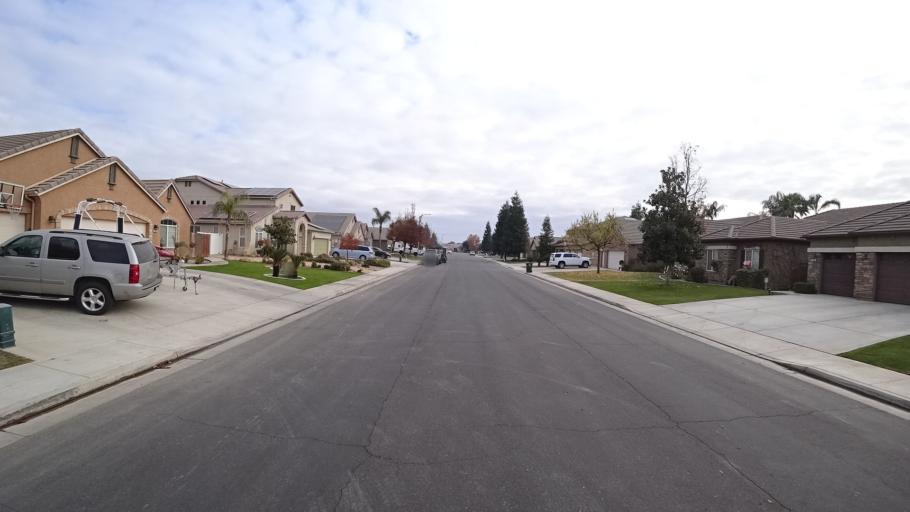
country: US
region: California
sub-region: Kern County
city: Rosedale
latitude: 35.2977
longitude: -119.1318
